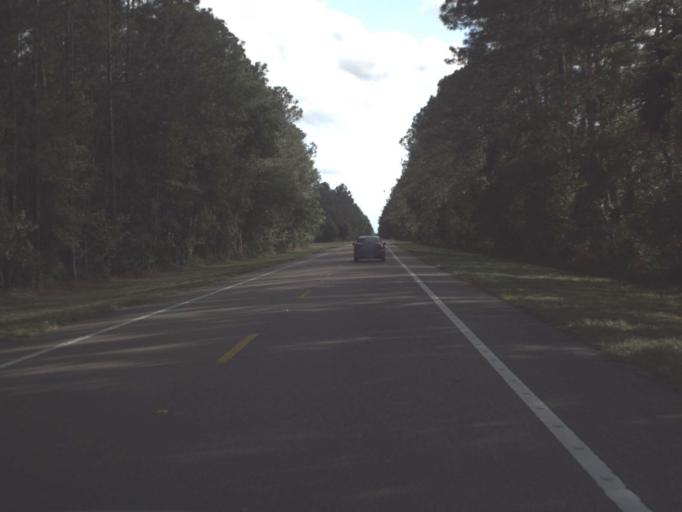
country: US
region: Florida
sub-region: Volusia County
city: Pierson
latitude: 29.3082
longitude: -81.3166
